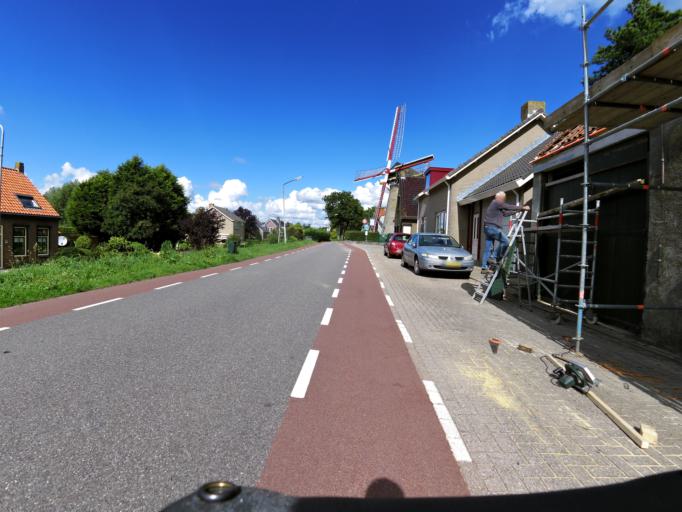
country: NL
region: South Holland
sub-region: Gemeente Goeree-Overflakkee
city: Middelharnis
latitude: 51.7320
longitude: 4.2368
